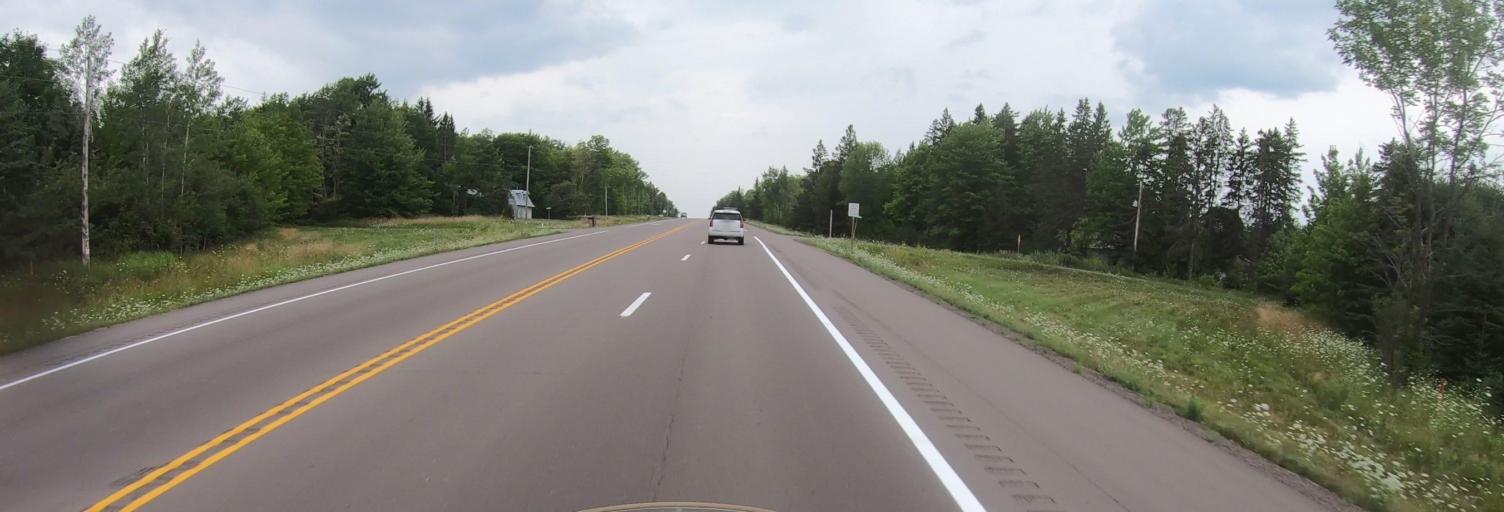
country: US
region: Michigan
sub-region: Houghton County
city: Dollar Bay
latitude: 46.9745
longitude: -88.4646
